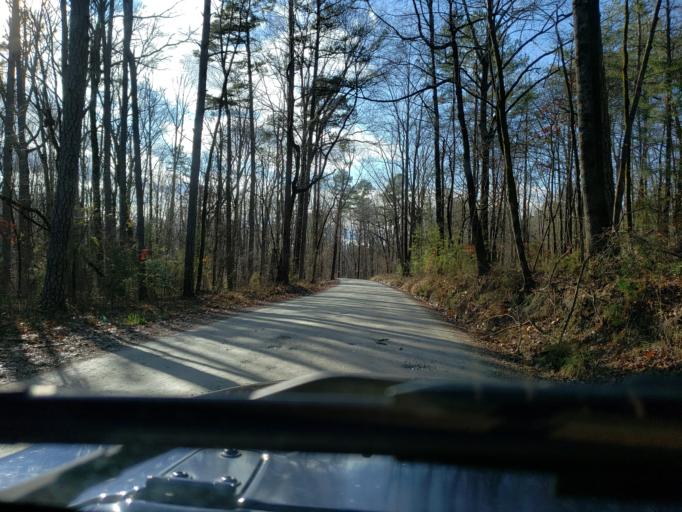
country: US
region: North Carolina
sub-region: Cleveland County
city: Kings Mountain
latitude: 35.1570
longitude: -81.3303
